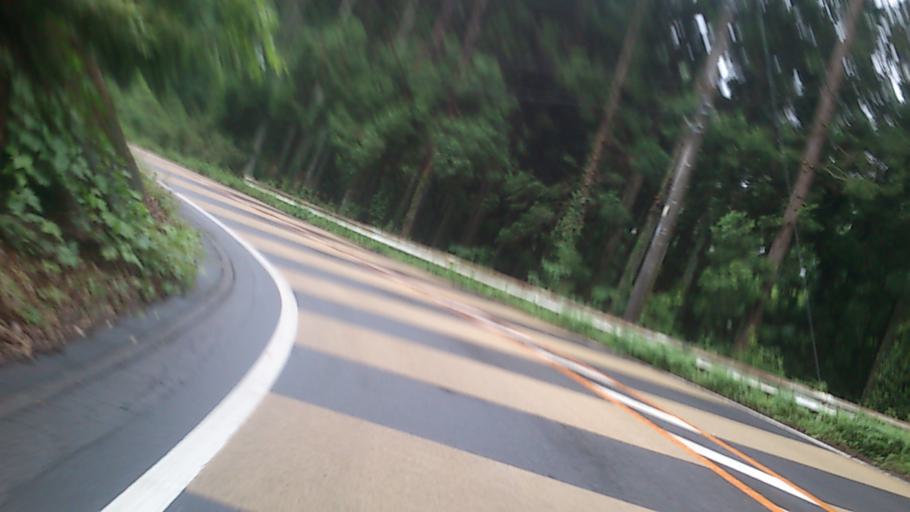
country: JP
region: Ibaraki
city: Omiya
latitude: 36.6293
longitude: 140.3416
